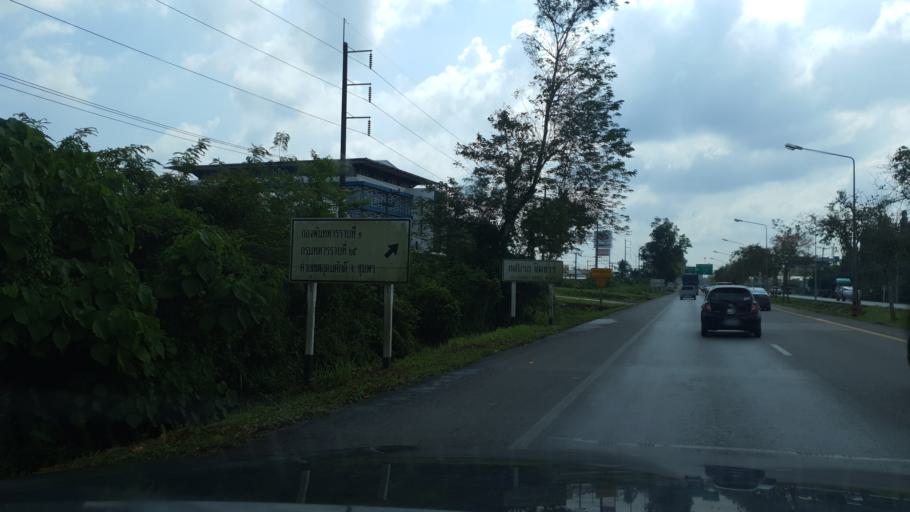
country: TH
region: Chumphon
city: Chumphon
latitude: 10.5264
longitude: 99.1164
